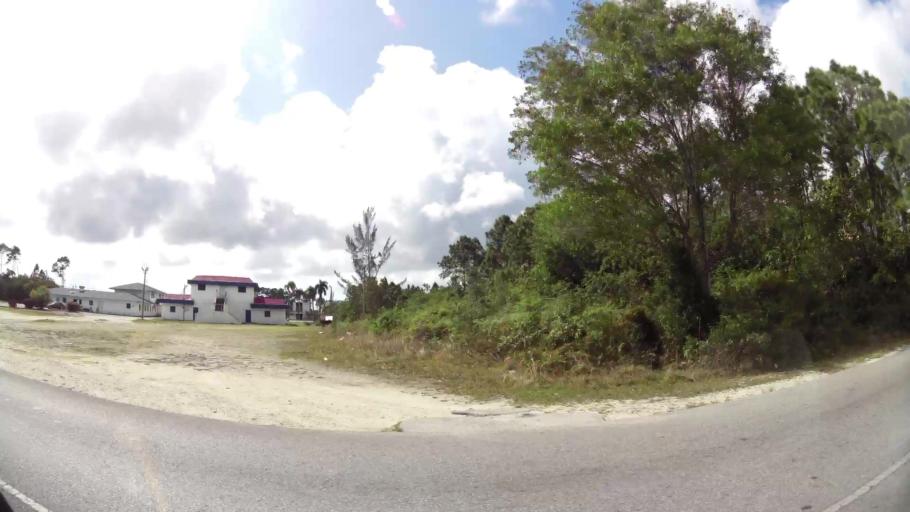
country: BS
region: Freeport
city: Freeport
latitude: 26.5355
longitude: -78.6971
